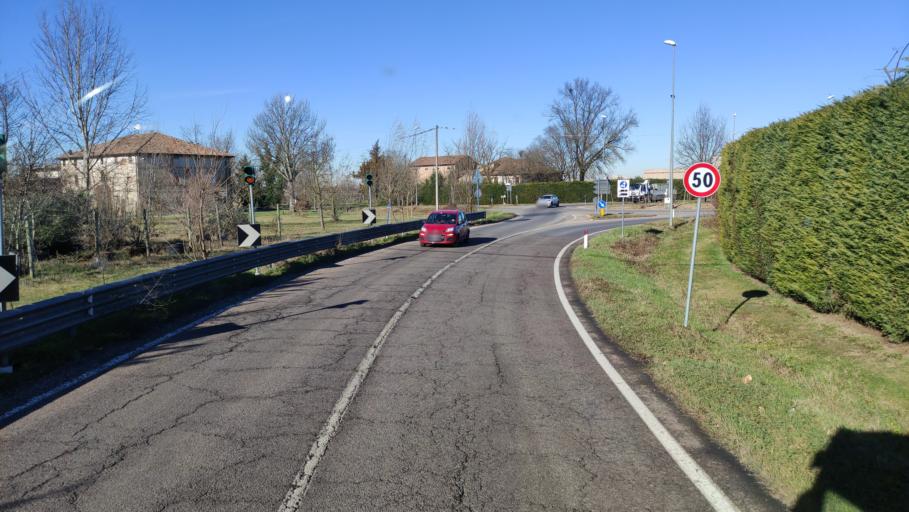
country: IT
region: Emilia-Romagna
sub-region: Provincia di Reggio Emilia
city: Rio Saliceto
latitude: 44.8084
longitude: 10.7828
